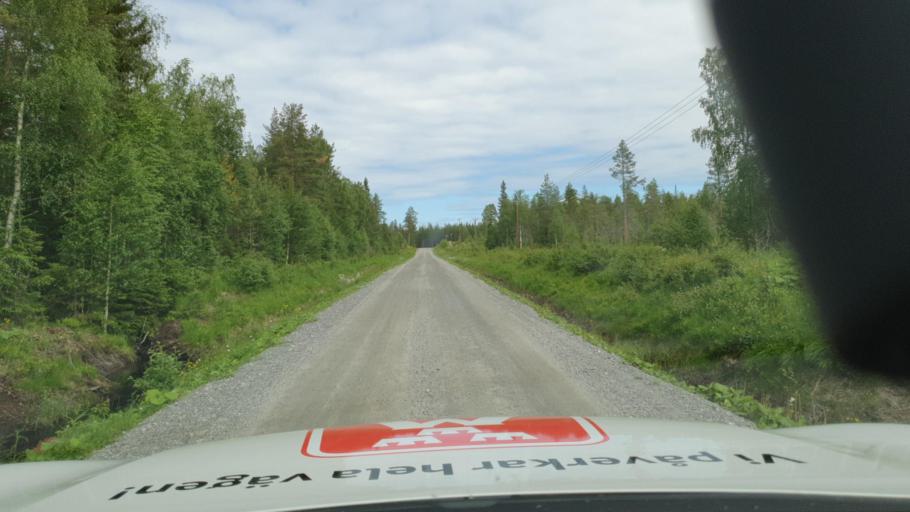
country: SE
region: Vaesterbotten
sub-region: Skelleftea Kommun
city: Langsele
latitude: 64.5458
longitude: 20.2832
